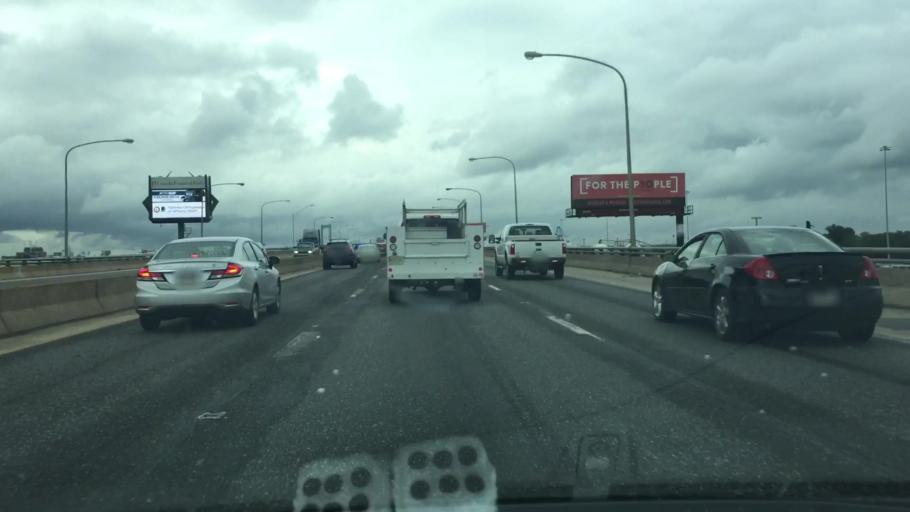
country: US
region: New Jersey
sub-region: Gloucester County
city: National Park
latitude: 39.8987
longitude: -75.1678
